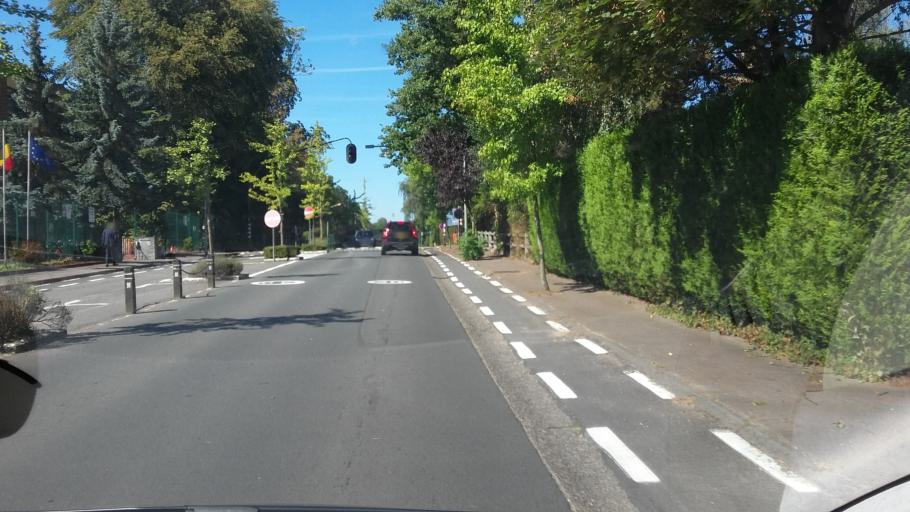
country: BE
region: Wallonia
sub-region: Province du Brabant Wallon
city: Waterloo
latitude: 50.7052
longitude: 4.4155
